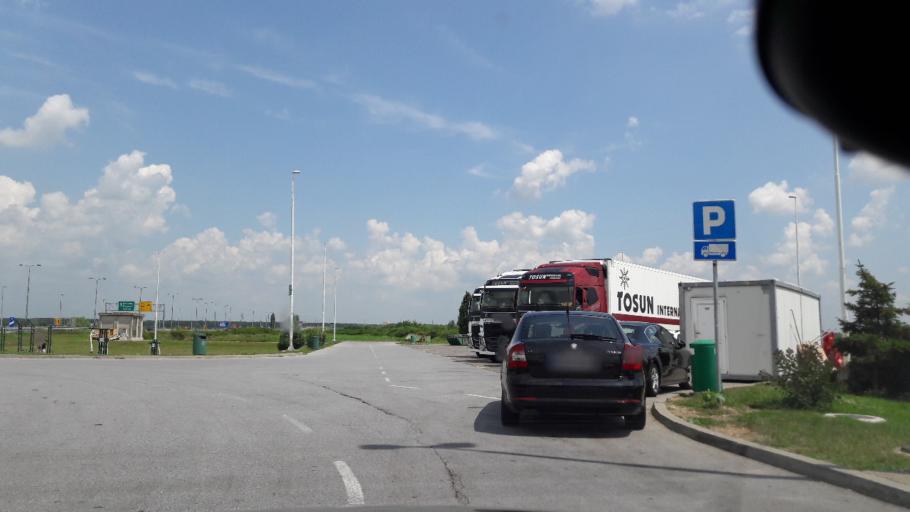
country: RS
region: Autonomna Pokrajina Vojvodina
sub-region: Sremski Okrug
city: Sid
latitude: 45.0476
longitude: 19.1985
